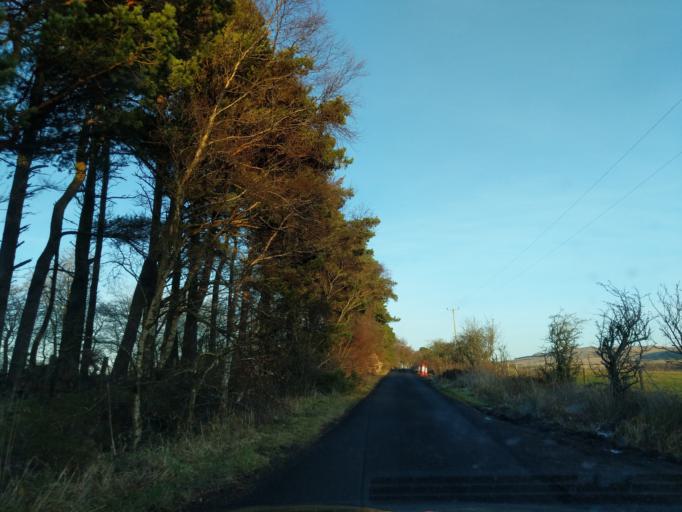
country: GB
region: Scotland
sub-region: Edinburgh
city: Balerno
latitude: 55.8594
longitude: -3.3500
